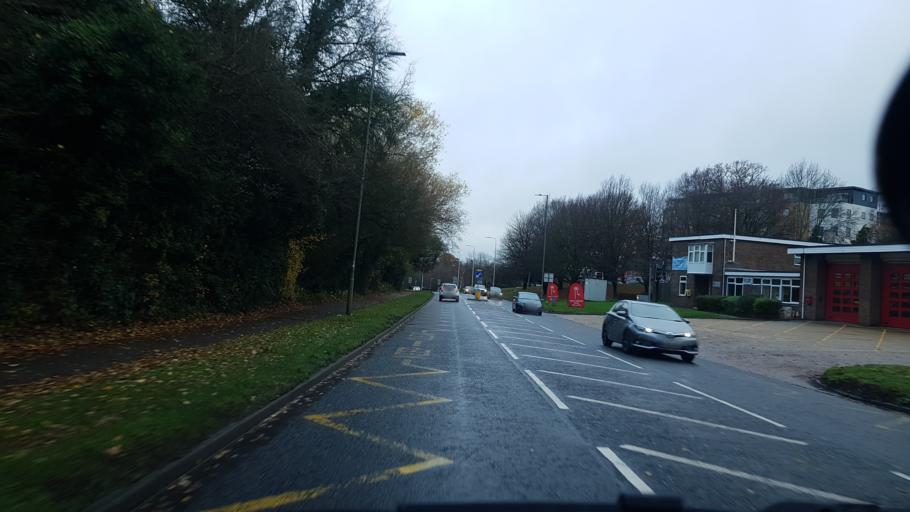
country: GB
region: England
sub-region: Bracknell Forest
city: Bracknell
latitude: 51.4114
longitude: -0.7566
